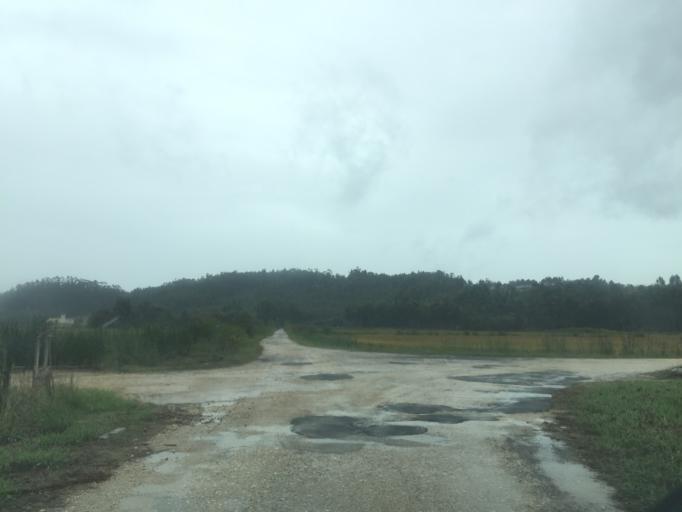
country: PT
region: Coimbra
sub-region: Figueira da Foz
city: Lavos
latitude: 40.0974
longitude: -8.8095
